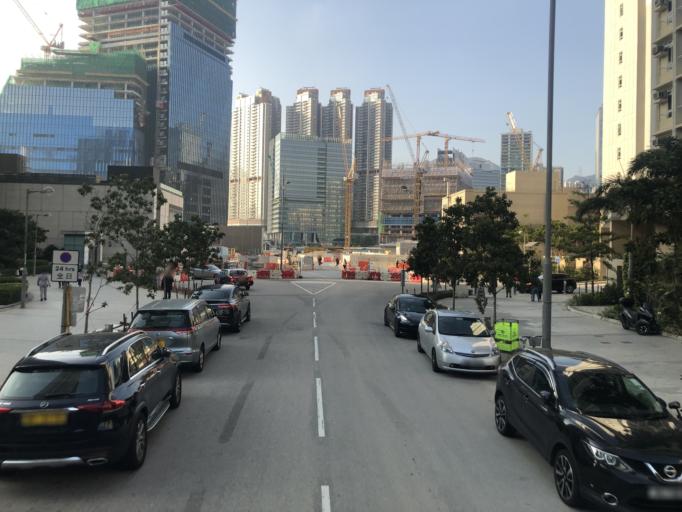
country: HK
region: Kowloon City
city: Kowloon
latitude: 22.3298
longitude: 114.2011
